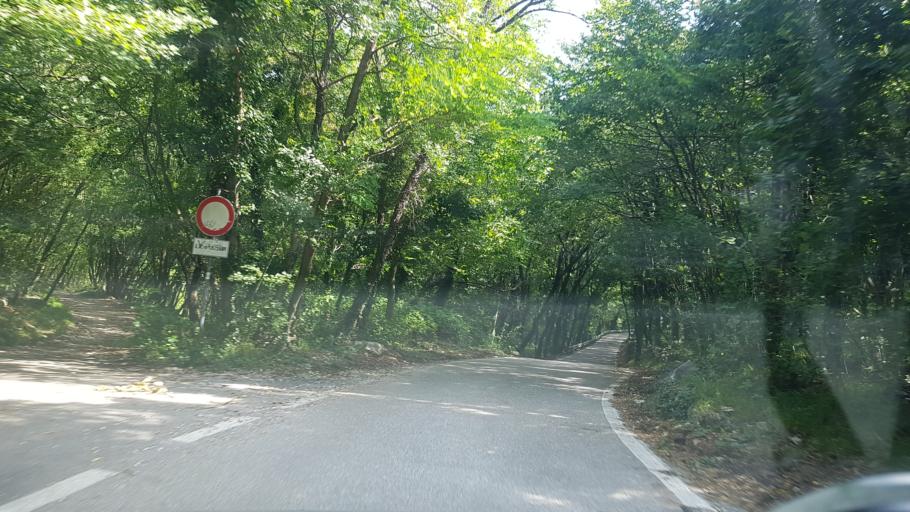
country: IT
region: Friuli Venezia Giulia
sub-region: Provincia di Trieste
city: Villa Opicina
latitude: 45.6745
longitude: 13.7977
